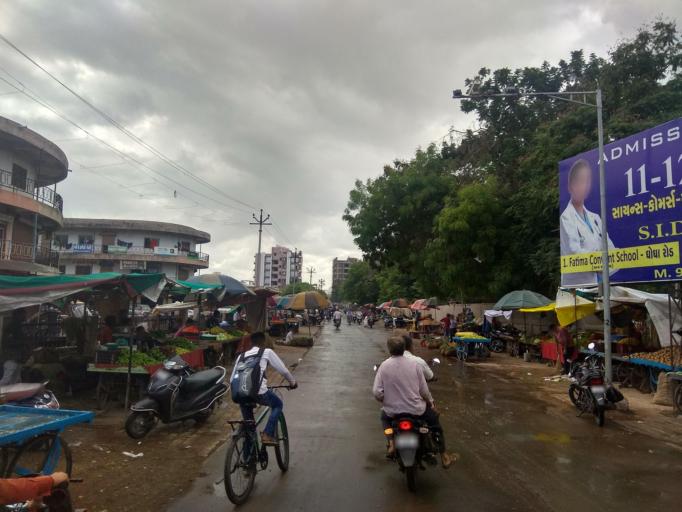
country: IN
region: Gujarat
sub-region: Bhavnagar
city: Bhavnagar
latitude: 21.7550
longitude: 72.1625
